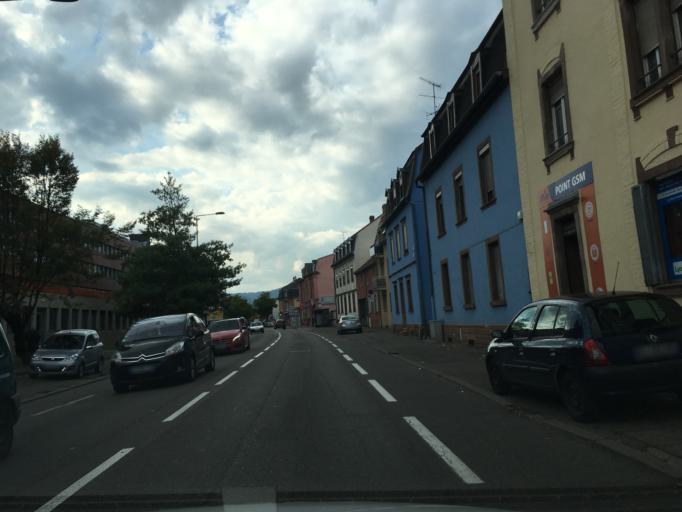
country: FR
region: Alsace
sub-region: Departement du Haut-Rhin
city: Colmar
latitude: 48.0843
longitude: 7.3443
